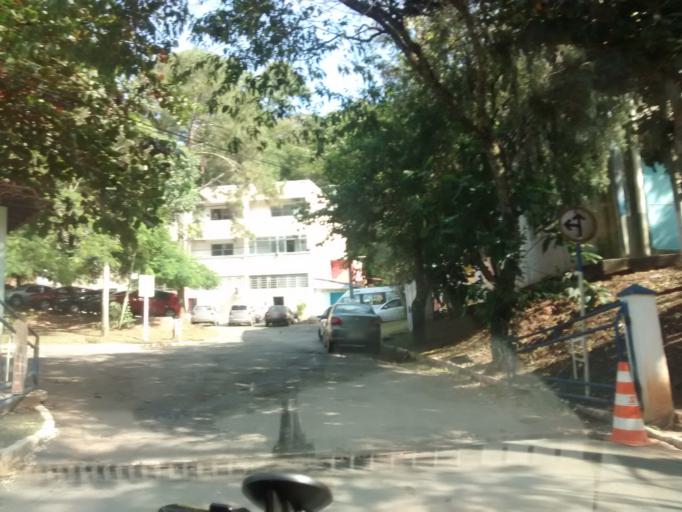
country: BR
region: Rio de Janeiro
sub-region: Miguel Pereira
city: Miguel Pereira
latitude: -22.4559
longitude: -43.4734
